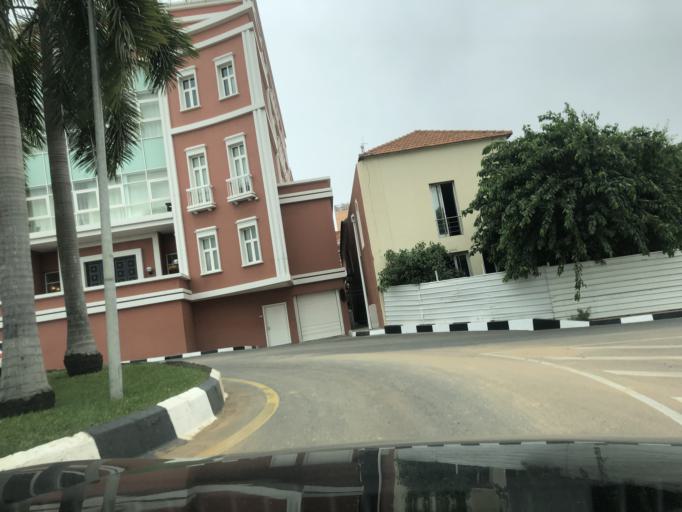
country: AO
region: Luanda
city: Luanda
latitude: -8.8191
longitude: 13.2251
